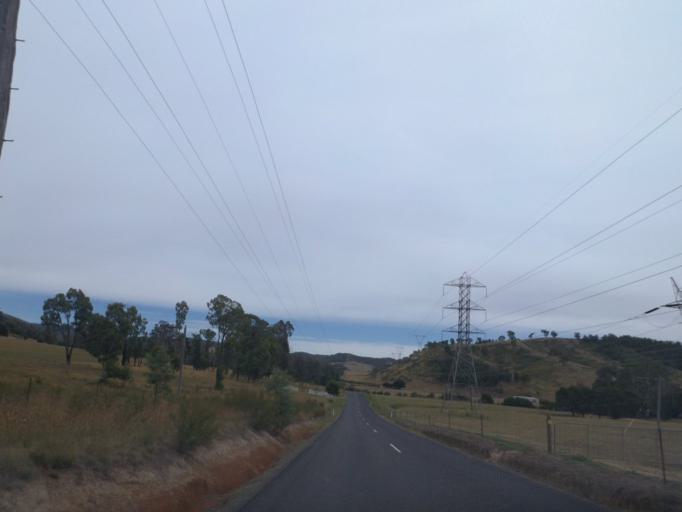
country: AU
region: Victoria
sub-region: Murrindindi
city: Alexandra
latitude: -37.3701
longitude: 145.5466
